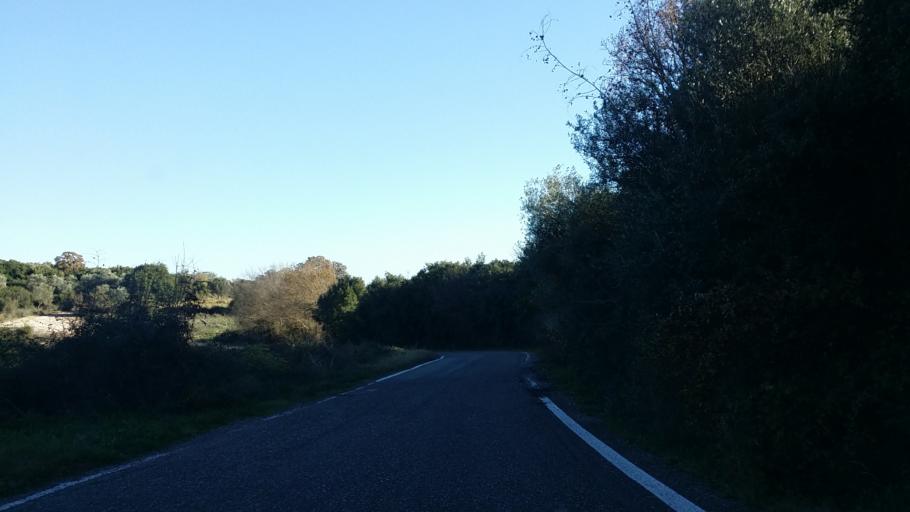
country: GR
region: West Greece
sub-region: Nomos Aitolias kai Akarnanias
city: Fitiai
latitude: 38.6230
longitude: 21.2112
